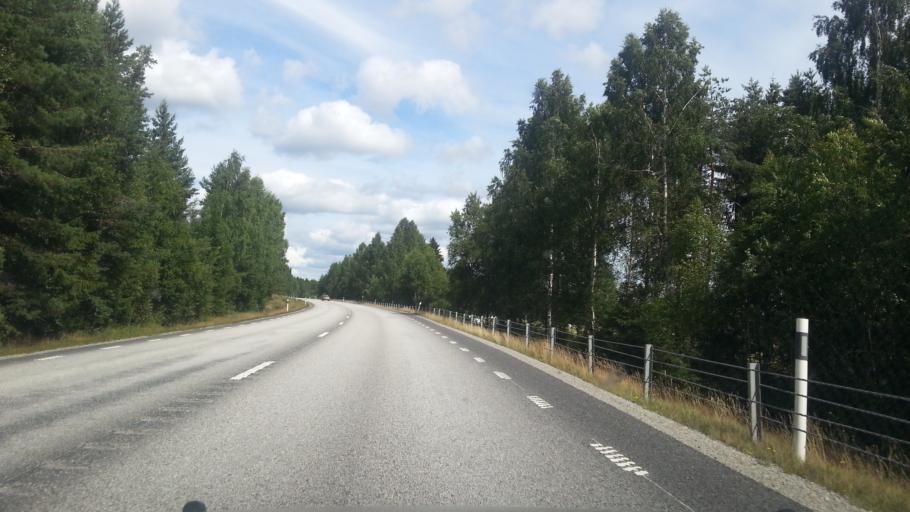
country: SE
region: OErebro
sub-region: Lindesbergs Kommun
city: Lindesberg
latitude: 59.6969
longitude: 15.3773
